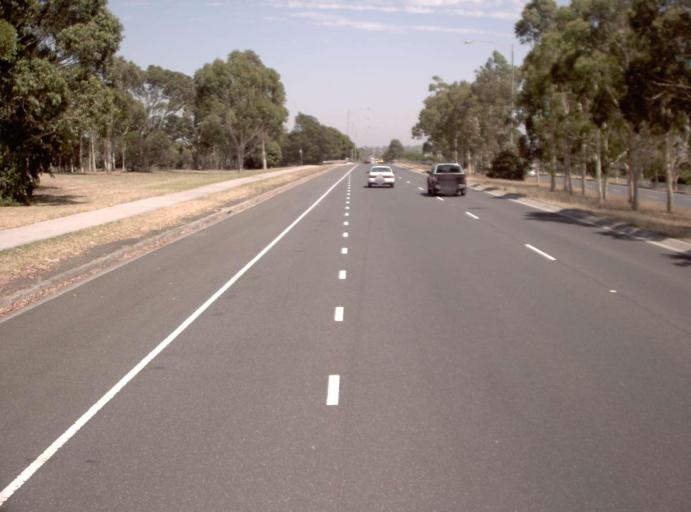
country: AU
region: Victoria
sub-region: Monash
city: Mulgrave
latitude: -37.9210
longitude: 145.1771
